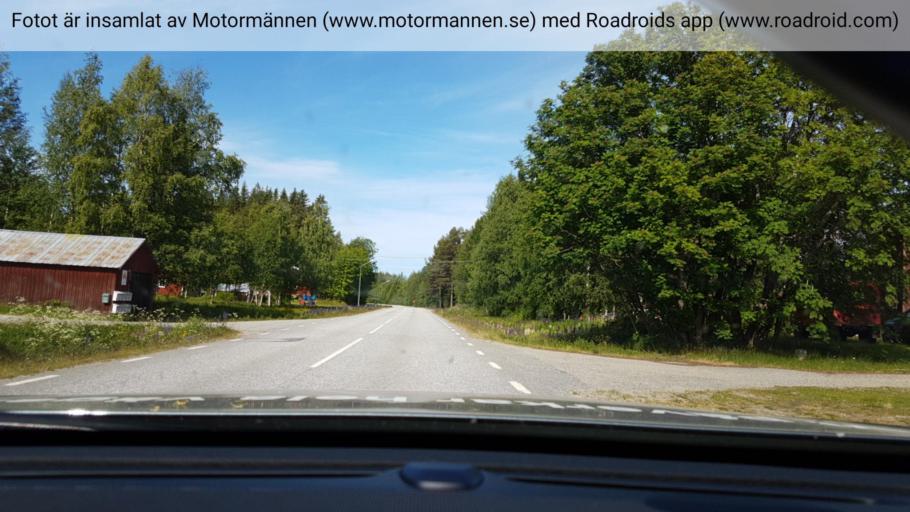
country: SE
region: Vaesterbotten
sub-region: Dorotea Kommun
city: Dorotea
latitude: 64.2512
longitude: 16.6598
